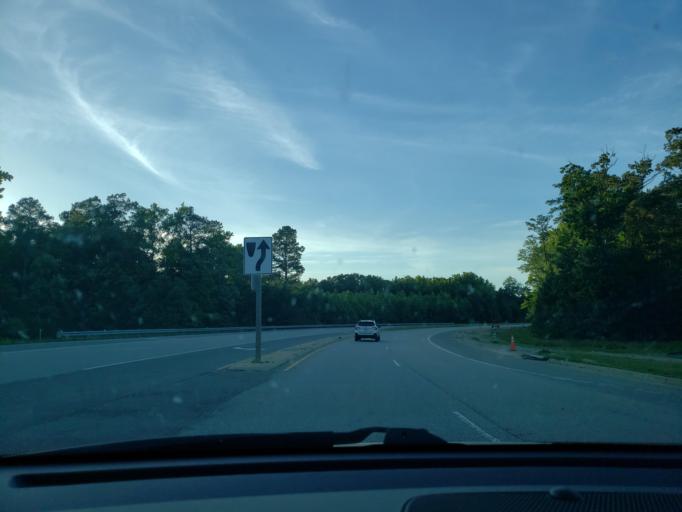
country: US
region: Virginia
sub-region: Henrico County
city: Fort Lee
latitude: 37.4861
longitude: -77.3423
